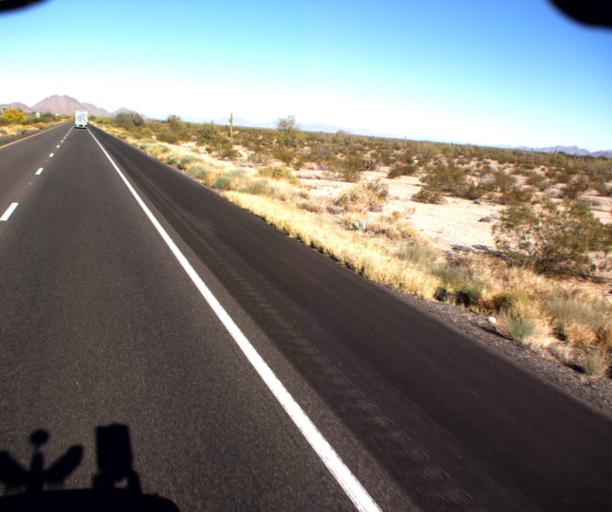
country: US
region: Arizona
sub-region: Maricopa County
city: Gila Bend
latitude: 32.8897
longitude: -112.4808
